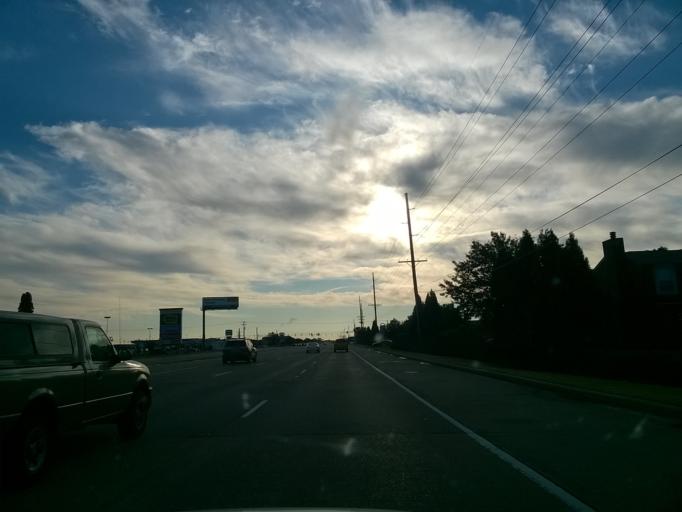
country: US
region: Indiana
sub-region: Vanderburgh County
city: Melody Hill
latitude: 37.9765
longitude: -87.4778
